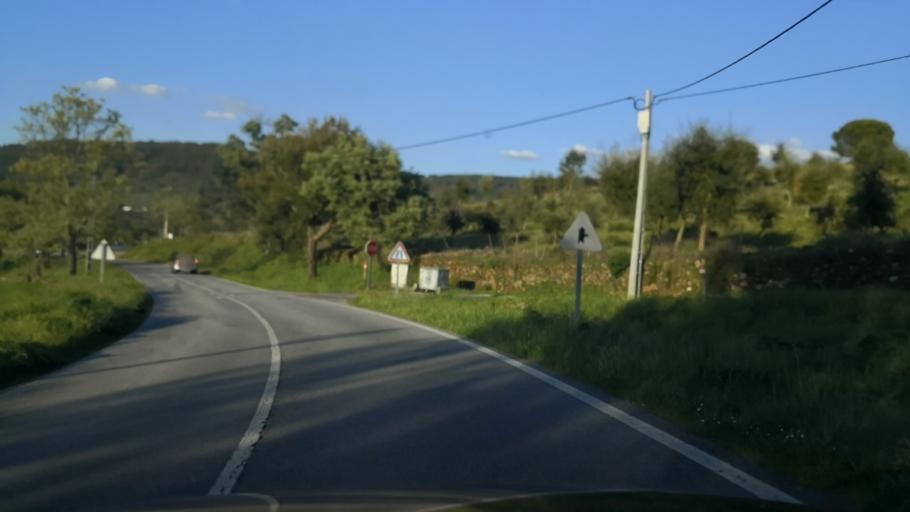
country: PT
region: Portalegre
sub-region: Marvao
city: Marvao
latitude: 39.3653
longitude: -7.3916
